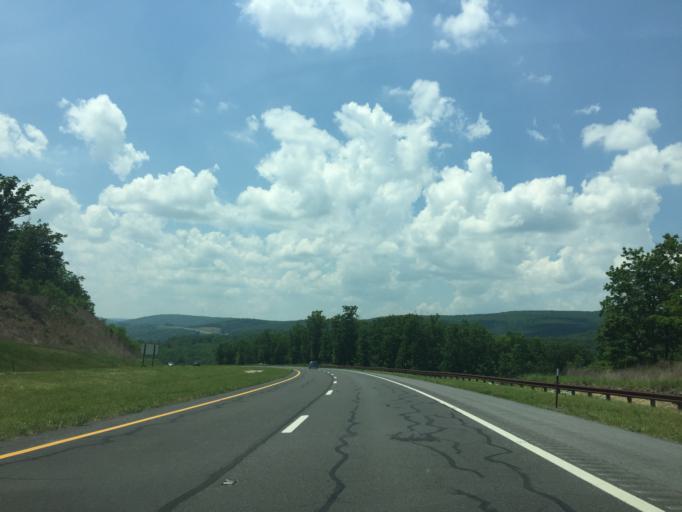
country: US
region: Virginia
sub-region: Shenandoah County
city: Woodstock
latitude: 39.0716
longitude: -78.6447
